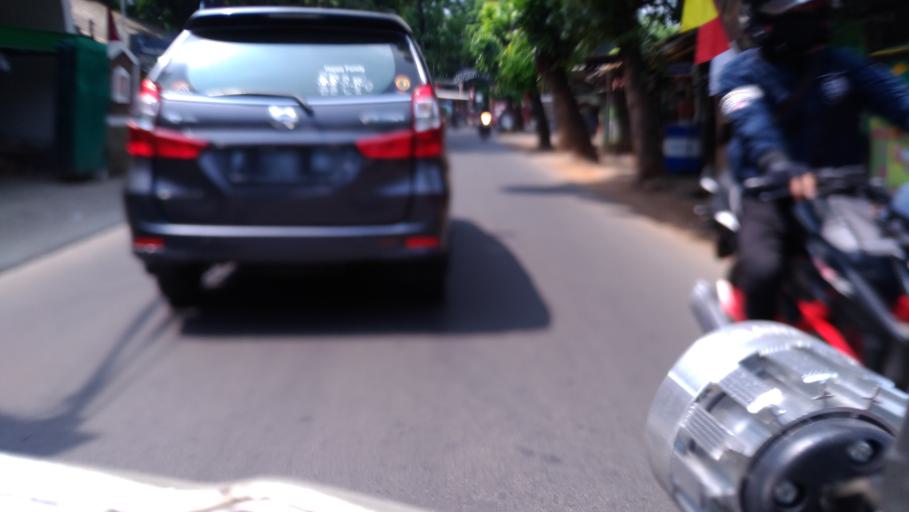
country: ID
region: West Java
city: Cileungsir
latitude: -6.3495
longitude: 106.8933
